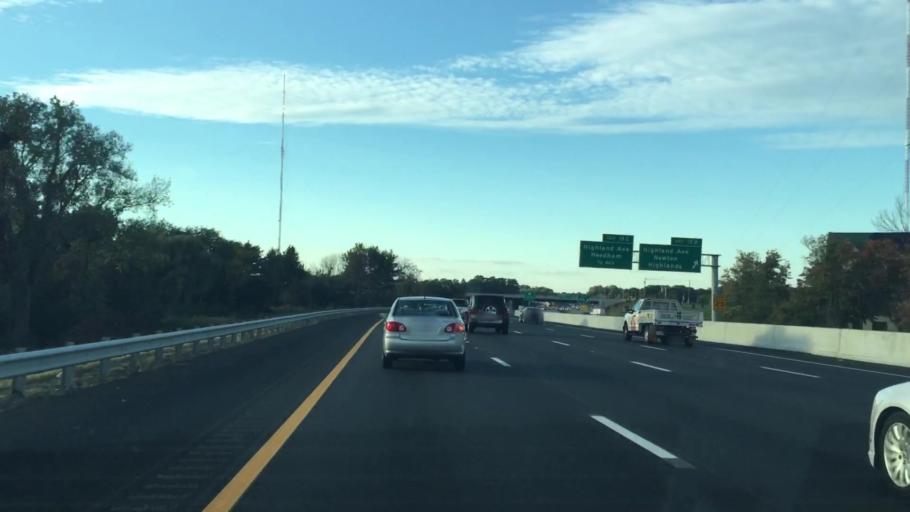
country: US
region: Massachusetts
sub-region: Norfolk County
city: Needham
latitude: 42.2992
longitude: -71.2220
